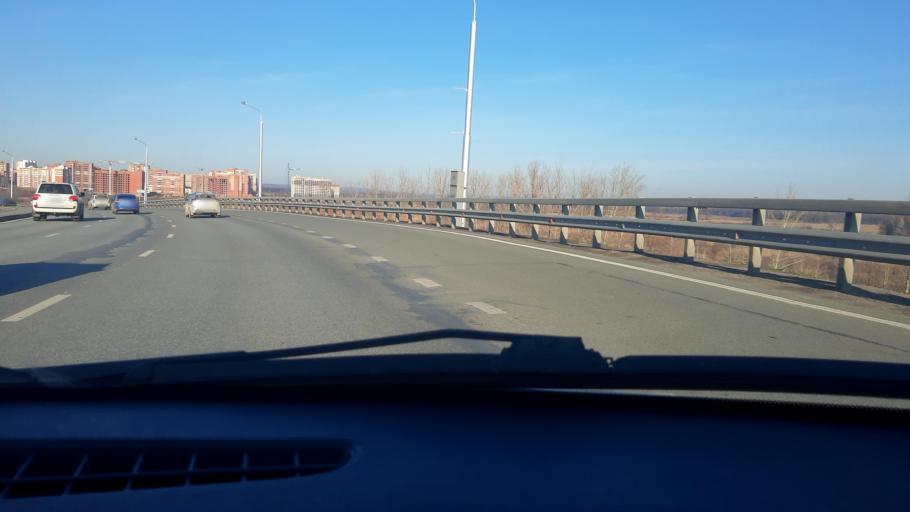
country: RU
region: Bashkortostan
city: Mikhaylovka
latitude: 54.7049
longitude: 55.8573
